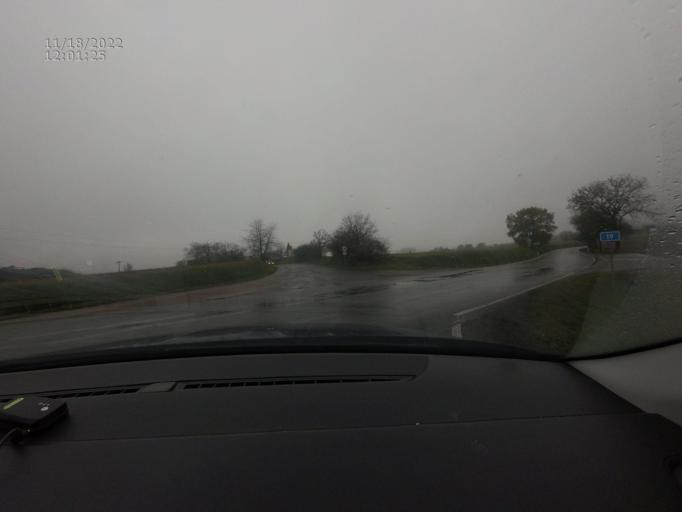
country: CZ
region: Plzensky
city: St'ahlavy
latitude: 49.6583
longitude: 13.4815
